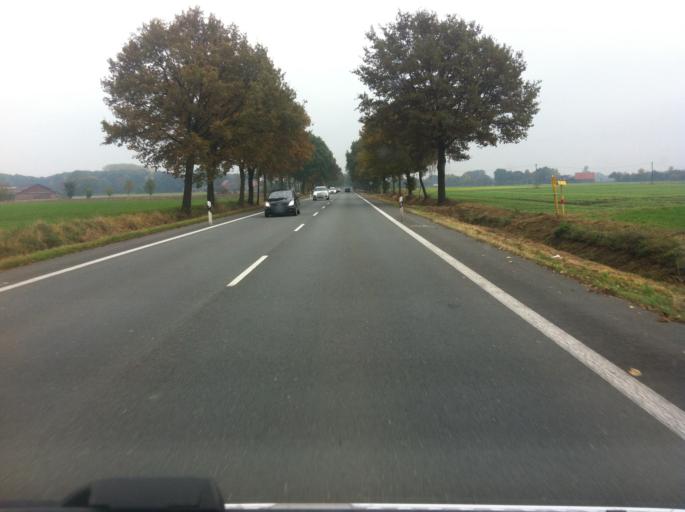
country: DE
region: North Rhine-Westphalia
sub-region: Regierungsbezirk Munster
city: Sudlohn
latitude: 51.9331
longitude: 6.8273
